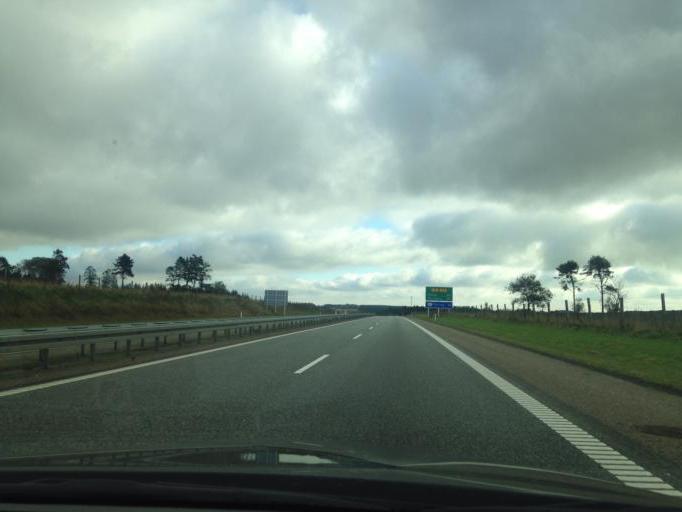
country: DK
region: South Denmark
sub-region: Vejle Kommune
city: Give
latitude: 55.8343
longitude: 9.3217
